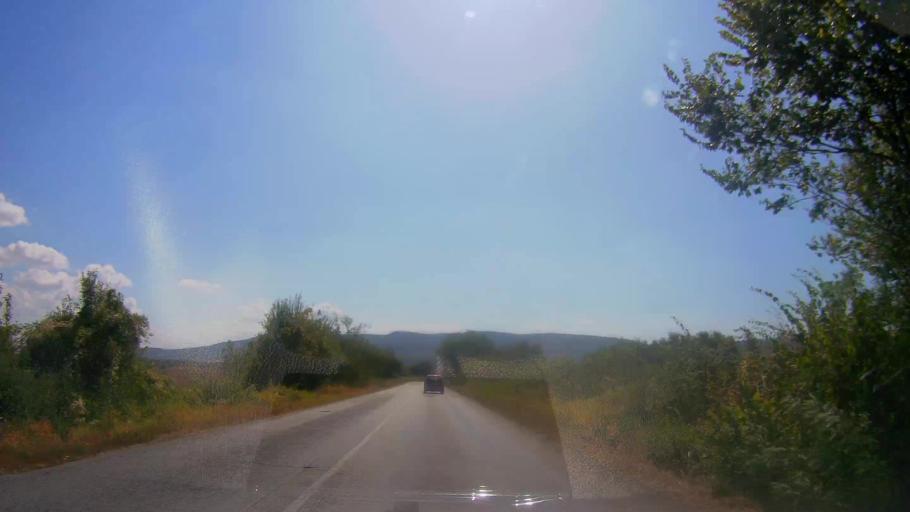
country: BG
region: Veliko Turnovo
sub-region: Obshtina Gorna Oryakhovitsa
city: Purvomaytsi
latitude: 43.1634
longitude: 25.6186
